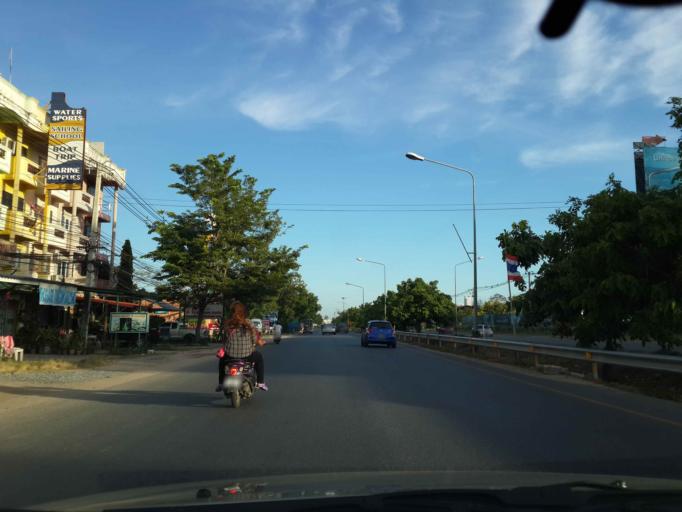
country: TH
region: Chon Buri
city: Phatthaya
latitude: 12.8326
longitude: 100.9137
